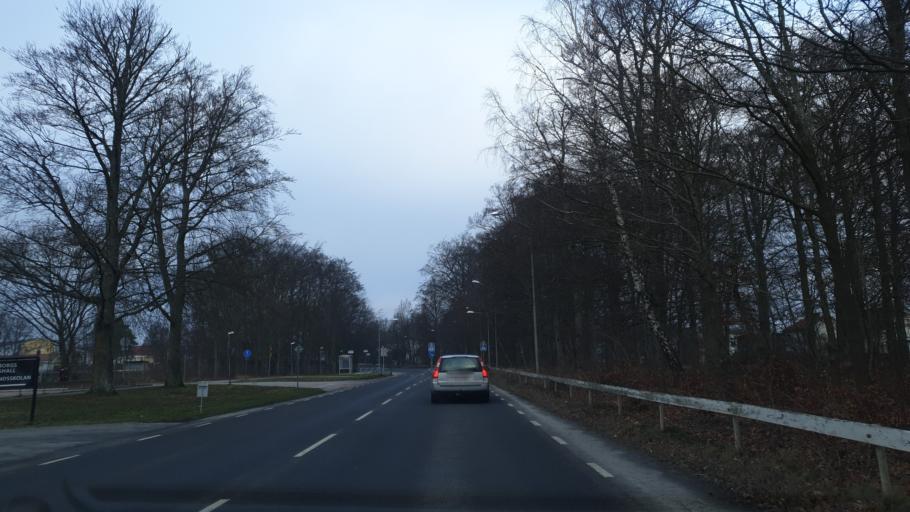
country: SE
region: Blekinge
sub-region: Solvesborgs Kommun
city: Soelvesborg
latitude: 56.0492
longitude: 14.5717
